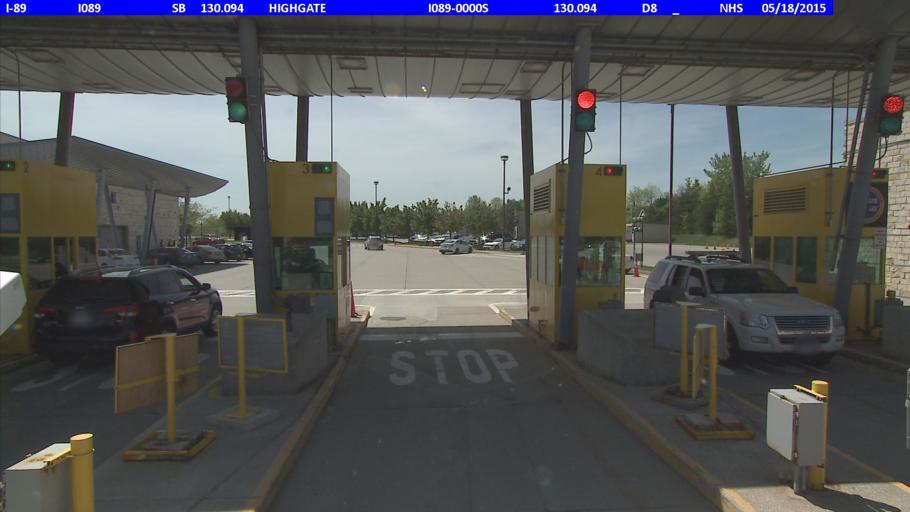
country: US
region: Vermont
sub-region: Franklin County
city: Swanton
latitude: 45.0131
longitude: -73.0857
